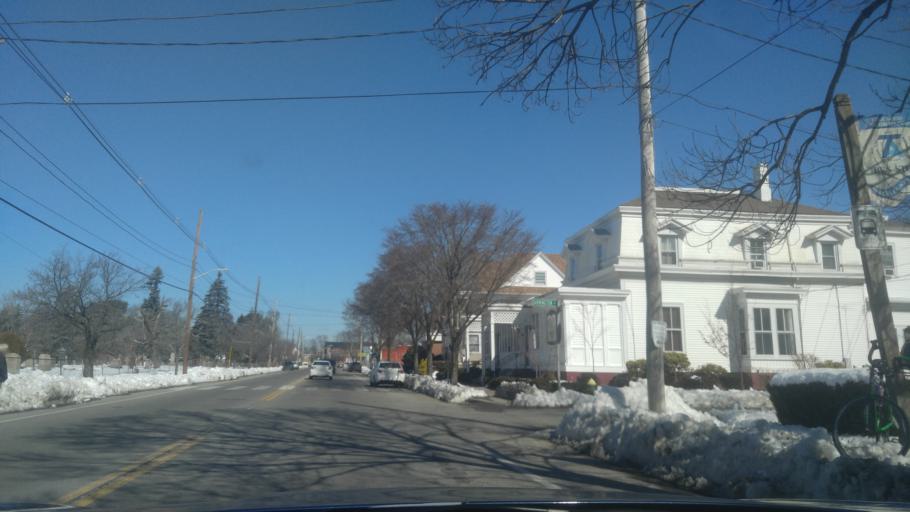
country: US
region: Rhode Island
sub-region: Providence County
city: Cranston
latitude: 41.7829
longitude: -71.4011
